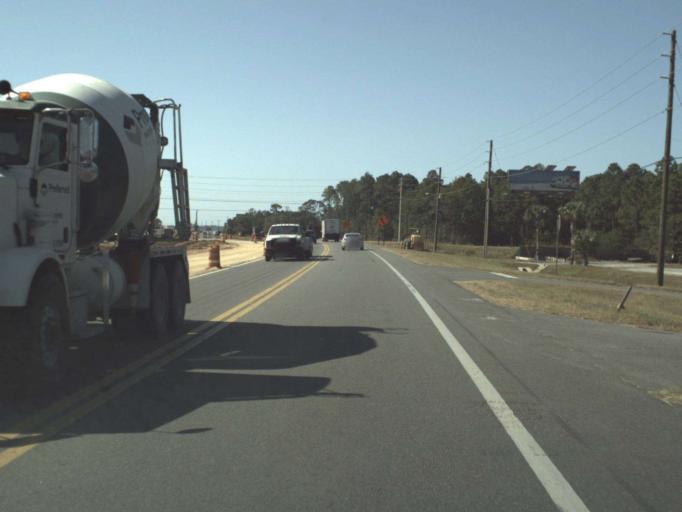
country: US
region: Florida
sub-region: Walton County
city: Freeport
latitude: 30.4370
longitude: -86.1510
